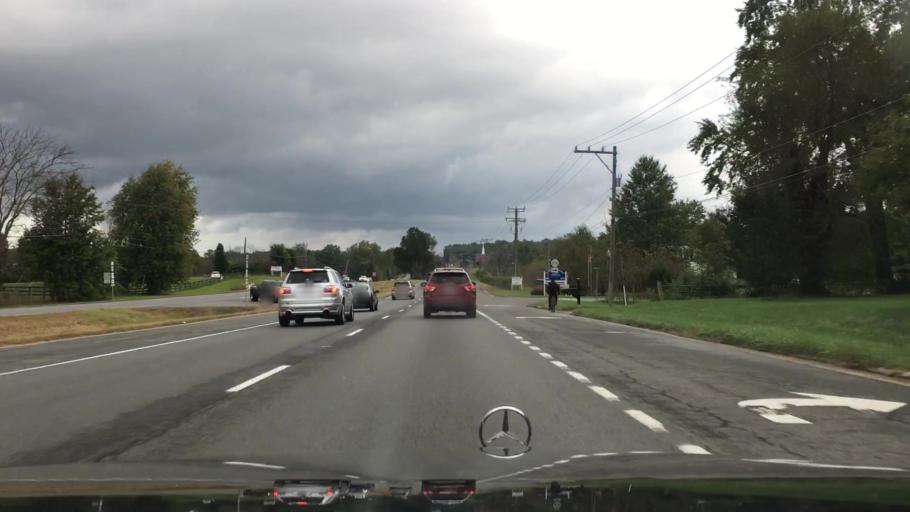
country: US
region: Virginia
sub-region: Fauquier County
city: New Baltimore
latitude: 38.7709
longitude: -77.6987
